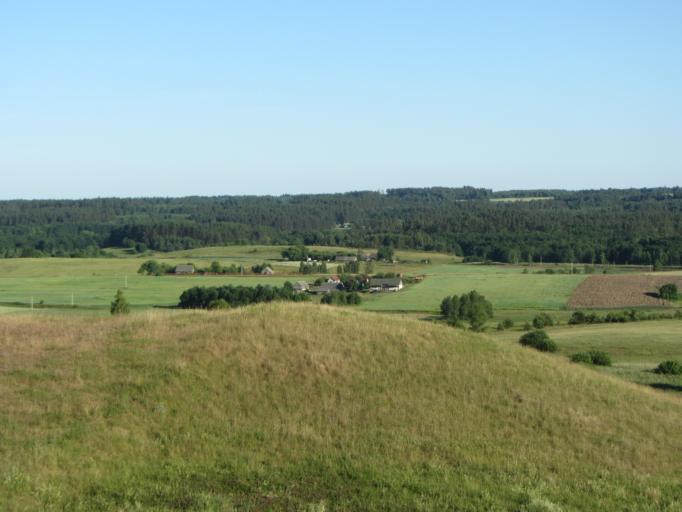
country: LT
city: Aukstadvaris
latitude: 54.5555
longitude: 24.4393
